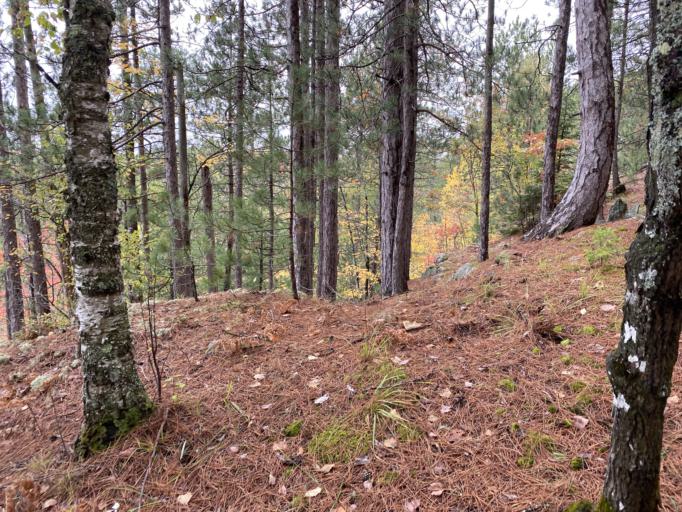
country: US
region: Michigan
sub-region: Marquette County
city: West Ishpeming
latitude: 46.5384
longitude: -87.9975
